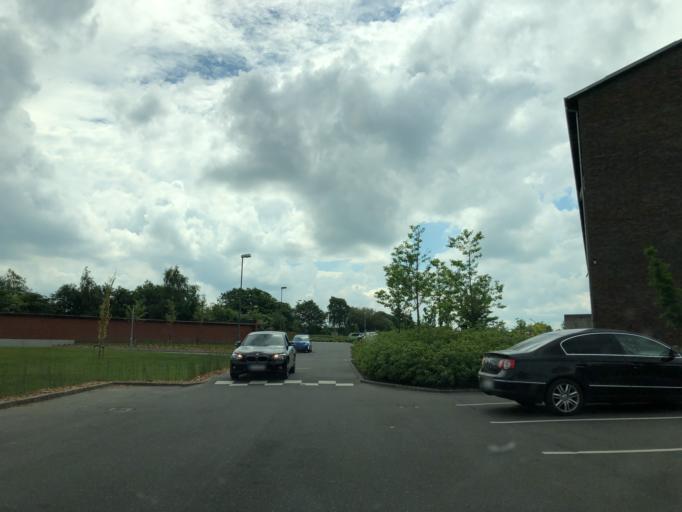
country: DK
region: Central Jutland
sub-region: Struer Kommune
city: Struer
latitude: 56.4859
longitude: 8.5919
